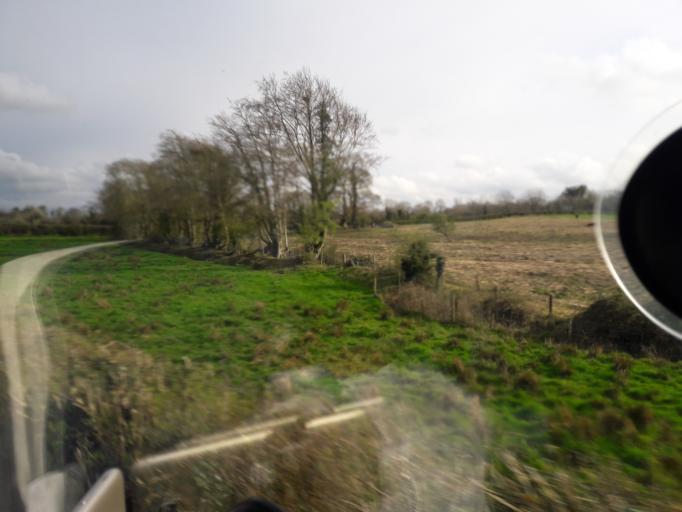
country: IE
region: Leinster
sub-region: An Mhi
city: Ballivor
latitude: 53.4736
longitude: -7.0178
